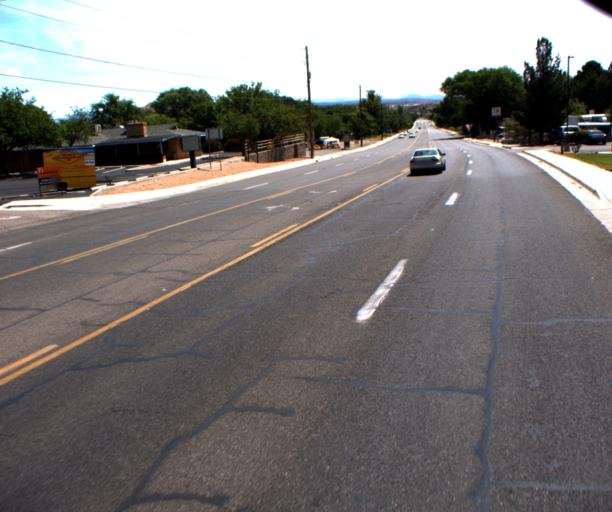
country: US
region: Arizona
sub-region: Yavapai County
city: Verde Village
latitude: 34.7213
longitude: -112.0012
